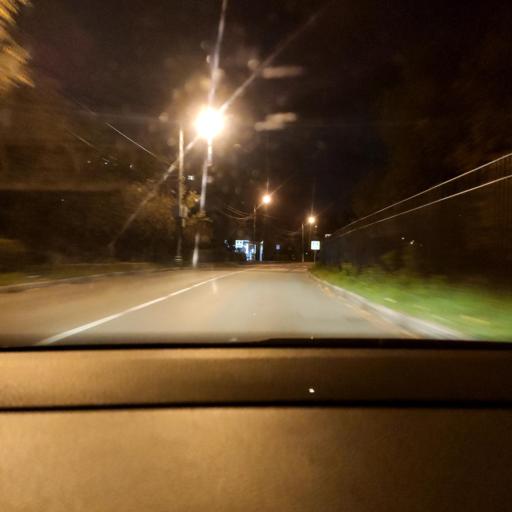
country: RU
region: Moscow
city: Khimki
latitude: 55.8961
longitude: 37.4162
